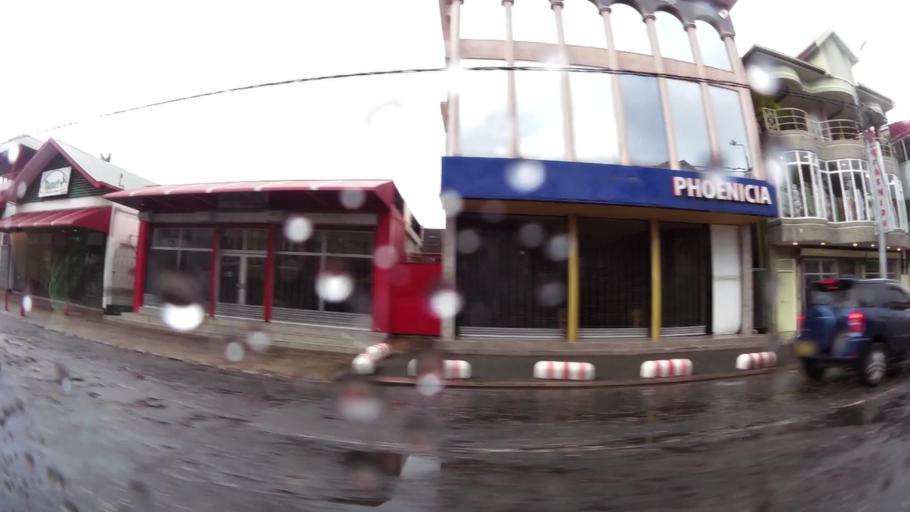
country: SR
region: Paramaribo
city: Paramaribo
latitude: 5.8283
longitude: -55.1610
